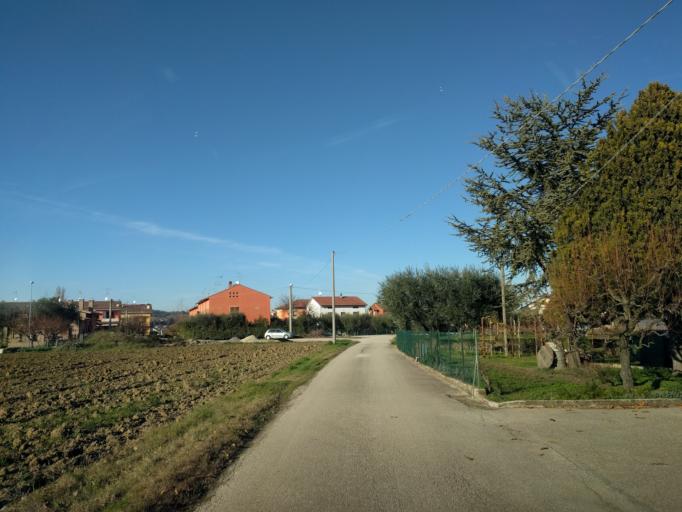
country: IT
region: The Marches
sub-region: Provincia di Pesaro e Urbino
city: Villanova
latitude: 43.7419
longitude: 12.9365
